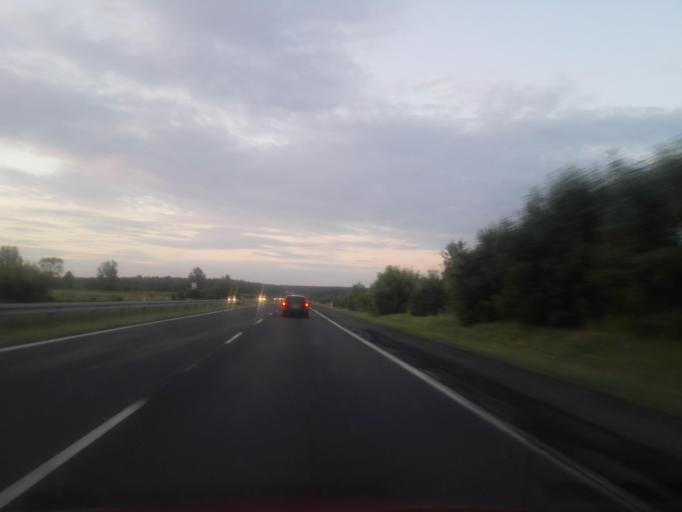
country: PL
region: Lodz Voivodeship
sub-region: Powiat radomszczanski
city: Gomunice
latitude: 51.1471
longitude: 19.4337
